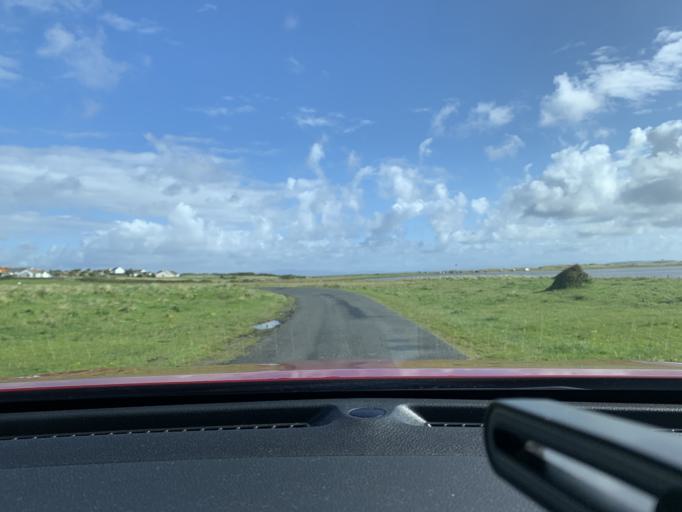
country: IE
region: Connaught
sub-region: Sligo
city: Strandhill
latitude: 54.3995
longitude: -8.5641
